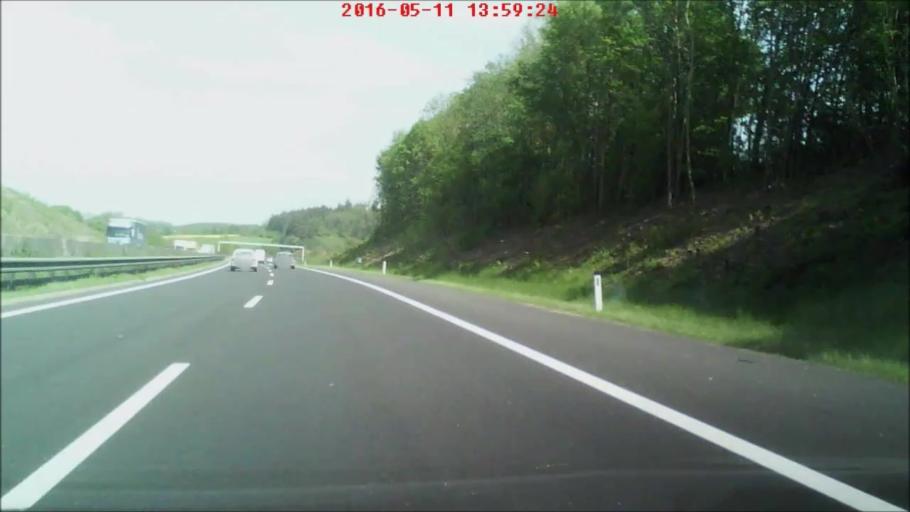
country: AT
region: Upper Austria
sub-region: Politischer Bezirk Grieskirchen
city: Bad Schallerbach
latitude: 48.1877
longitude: 13.9474
